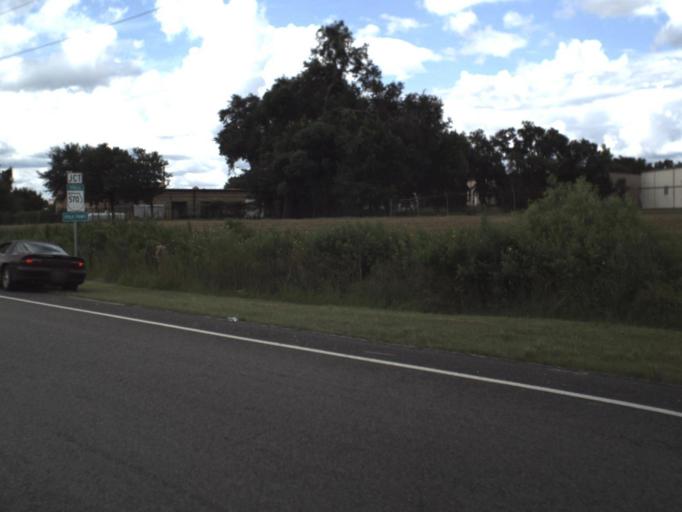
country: US
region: Florida
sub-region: Polk County
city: Highland City
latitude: 27.9972
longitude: -81.8995
